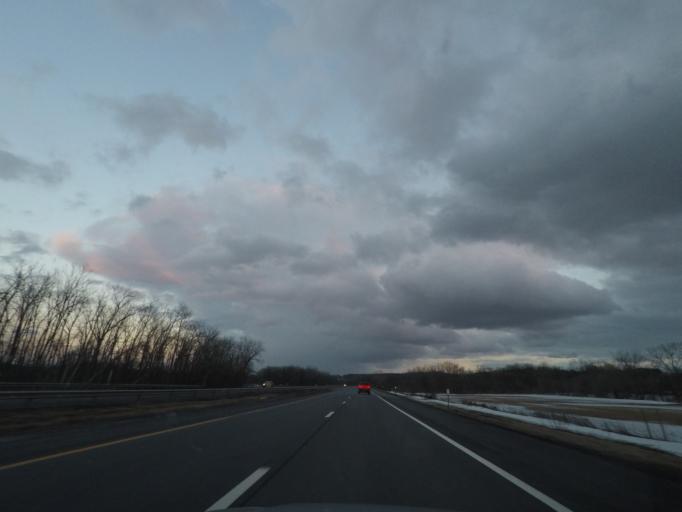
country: US
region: New York
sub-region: Montgomery County
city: Tribes Hill
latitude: 42.9333
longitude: -74.3194
